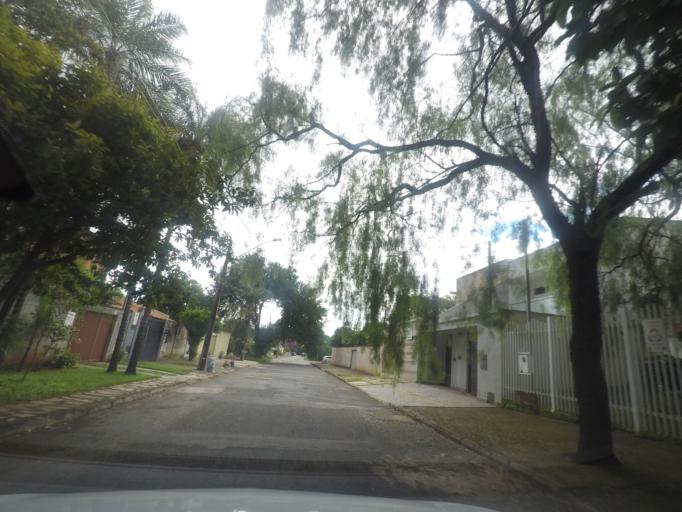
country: BR
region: Goias
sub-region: Goiania
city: Goiania
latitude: -16.6401
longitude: -49.2243
